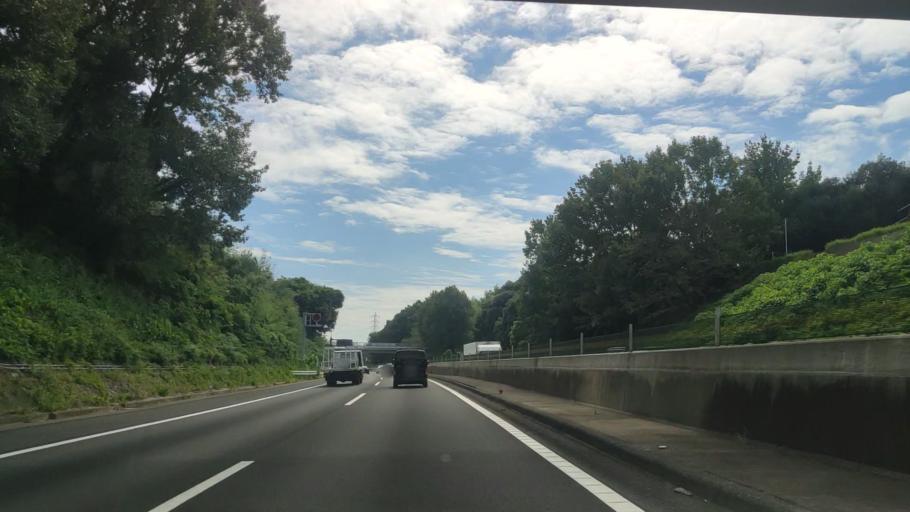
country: JP
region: Aichi
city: Okazaki
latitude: 35.0046
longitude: 137.1757
